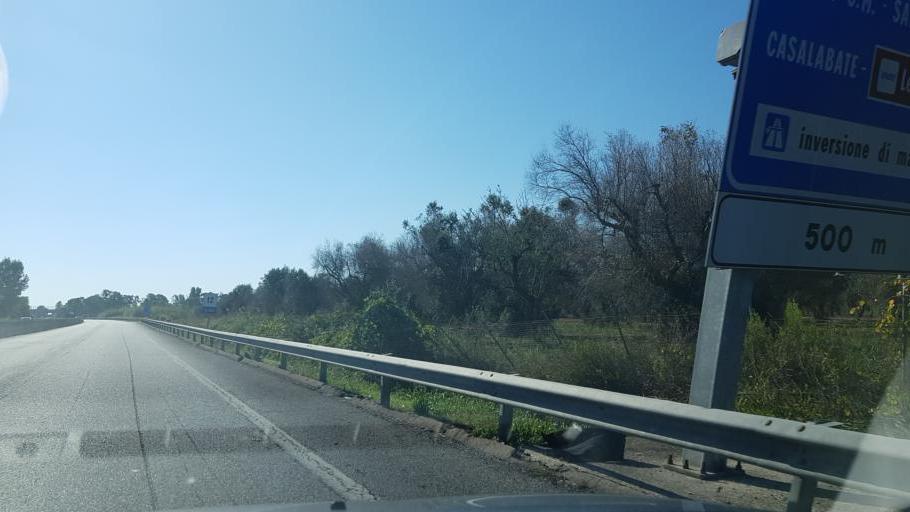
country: IT
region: Apulia
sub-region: Provincia di Brindisi
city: San Pietro Vernotico
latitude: 40.5262
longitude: 18.0131
